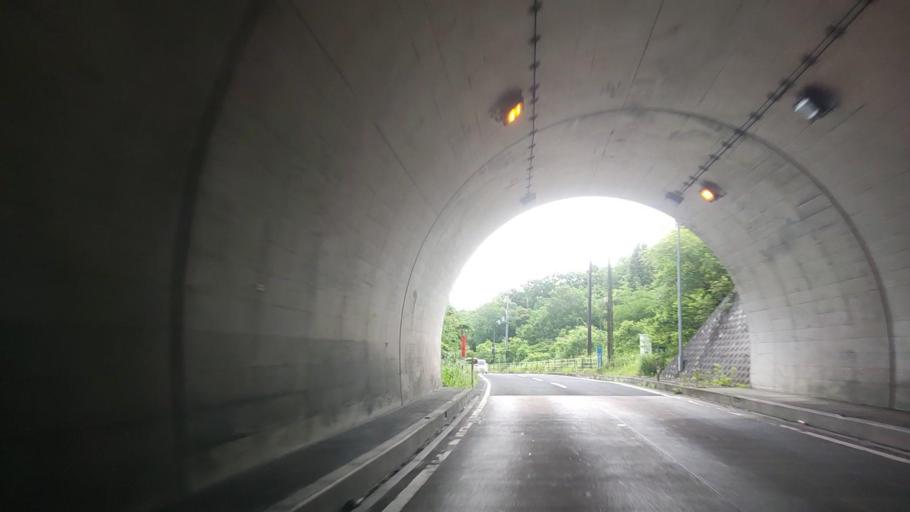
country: JP
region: Kyoto
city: Miyazu
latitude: 35.5830
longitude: 135.1153
